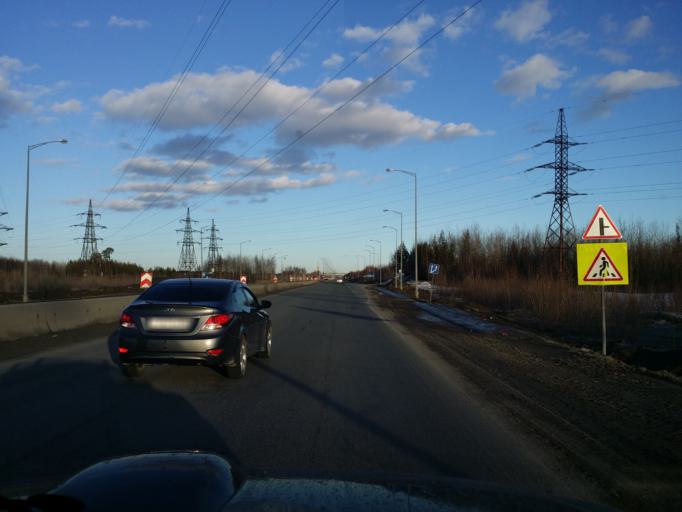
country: RU
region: Khanty-Mansiyskiy Avtonomnyy Okrug
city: Nizhnevartovsk
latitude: 60.9856
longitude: 76.4751
